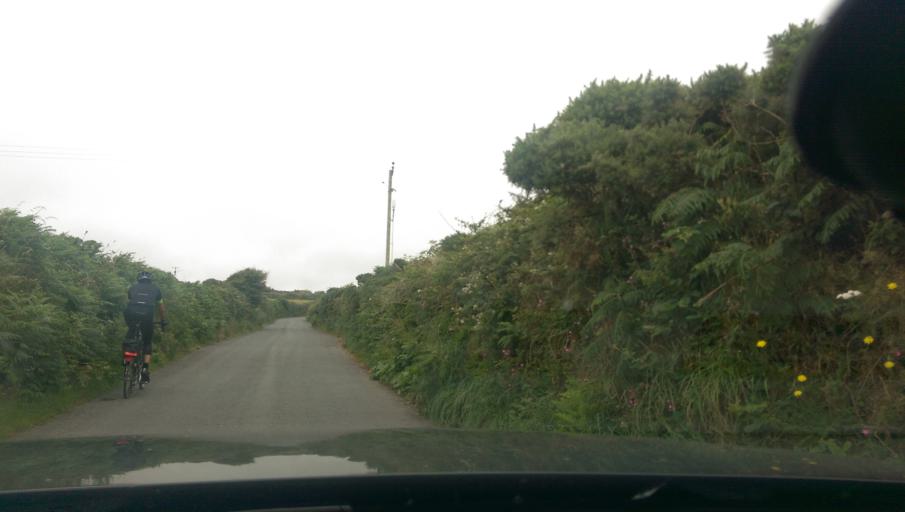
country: GB
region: England
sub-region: Cornwall
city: St. Buryan
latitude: 50.0954
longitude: -5.6484
